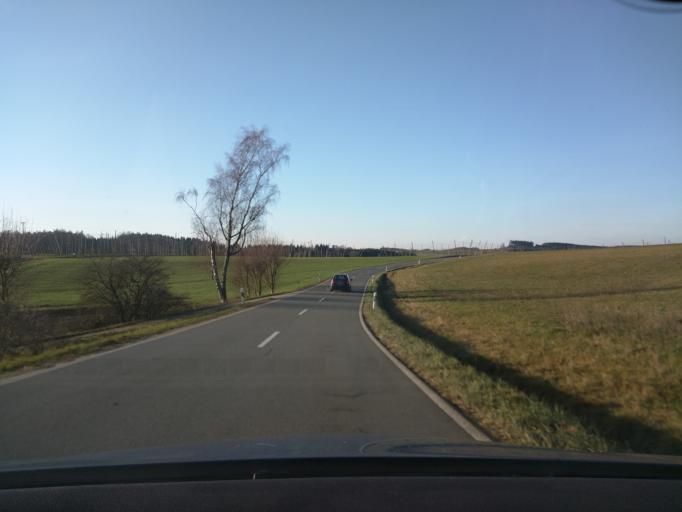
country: DE
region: Bavaria
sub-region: Upper Bavaria
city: Au in der Hallertau
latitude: 48.5730
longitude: 11.7023
